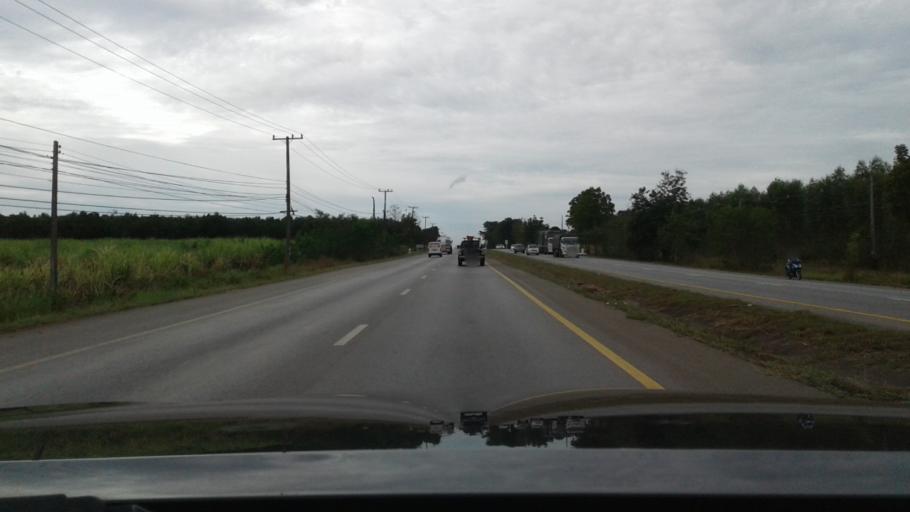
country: TH
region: Changwat Udon Thani
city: Non Sa-at
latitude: 17.0271
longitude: 102.9056
